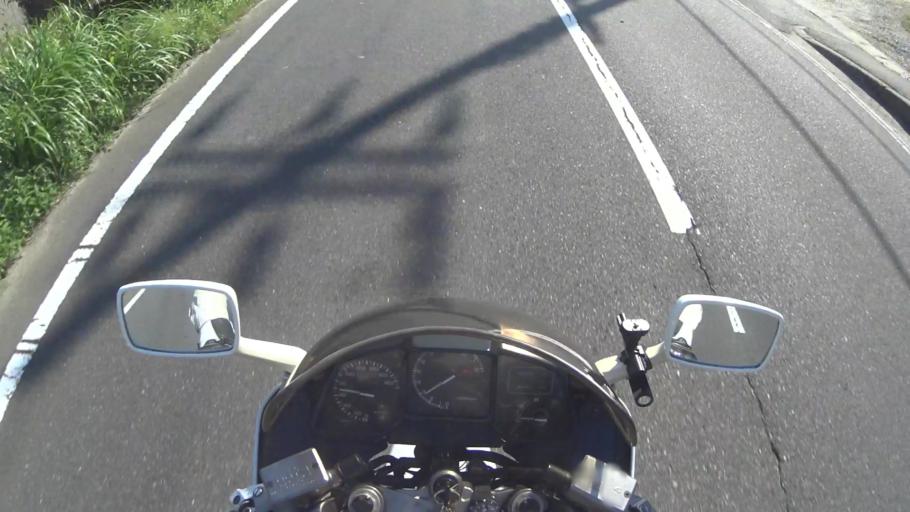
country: JP
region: Kyoto
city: Miyazu
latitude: 35.7365
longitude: 135.1002
